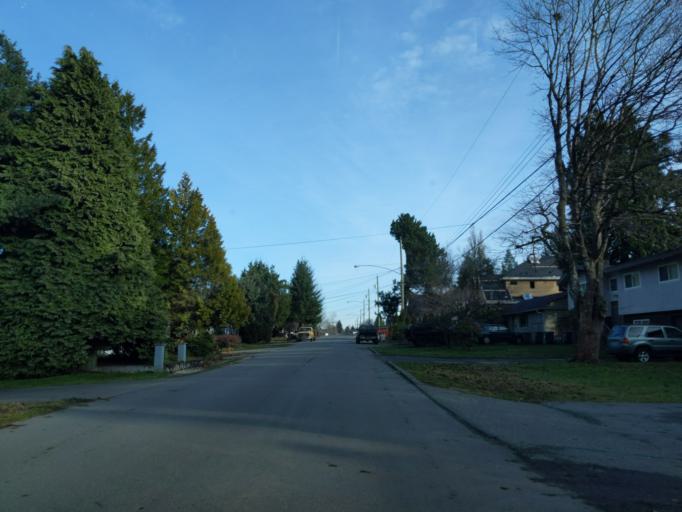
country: CA
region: British Columbia
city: New Westminster
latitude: 49.1970
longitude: -122.8617
